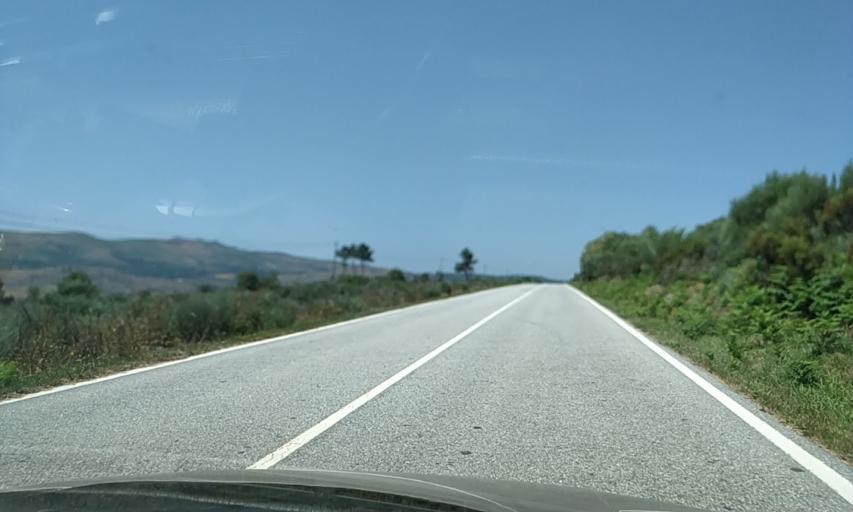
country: PT
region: Viseu
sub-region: Castro Daire
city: Castro Daire
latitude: 40.9548
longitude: -7.8894
